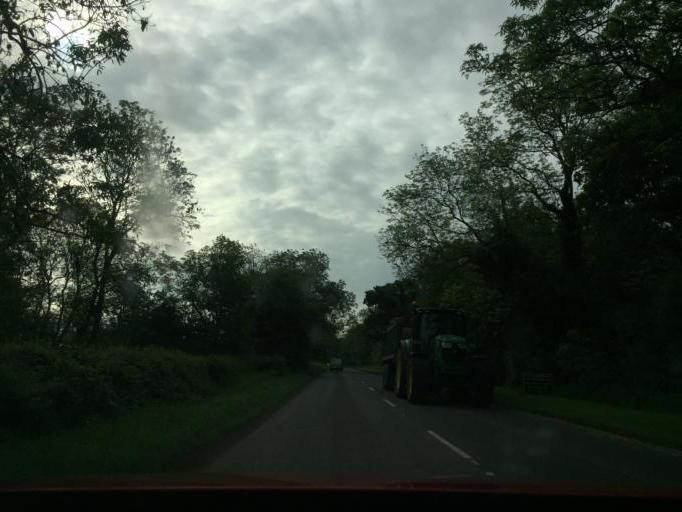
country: GB
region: England
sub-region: Leicestershire
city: Lutterworth
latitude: 52.4540
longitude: -1.2701
